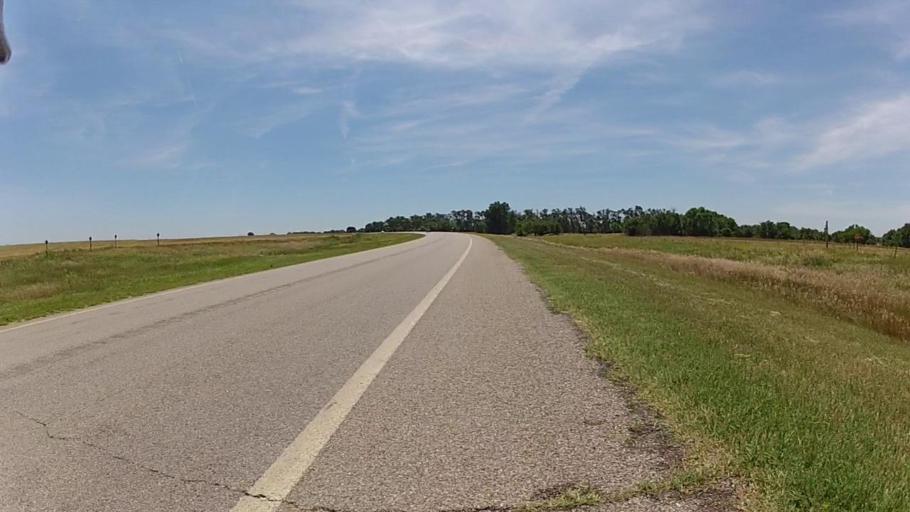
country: US
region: Kansas
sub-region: Barber County
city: Medicine Lodge
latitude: 37.2568
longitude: -98.5240
